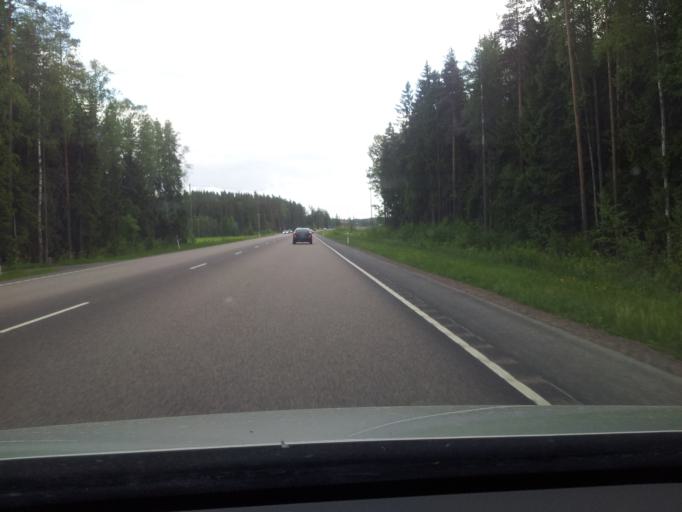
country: FI
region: Kymenlaakso
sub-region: Kouvola
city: Elimaeki
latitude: 60.8334
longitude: 26.5400
